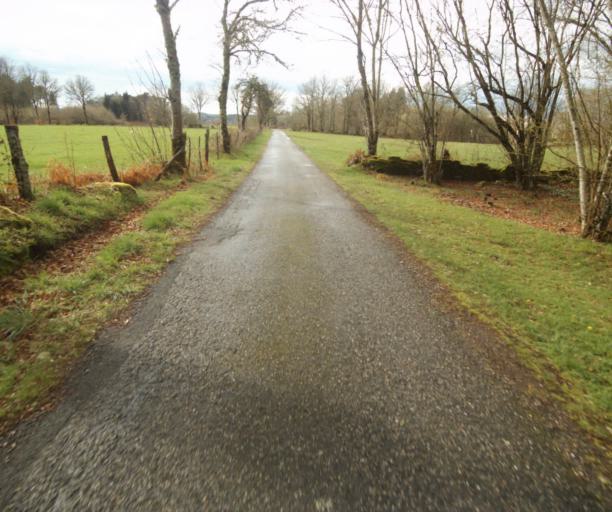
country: FR
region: Limousin
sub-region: Departement de la Correze
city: Saint-Privat
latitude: 45.2420
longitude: 2.0063
